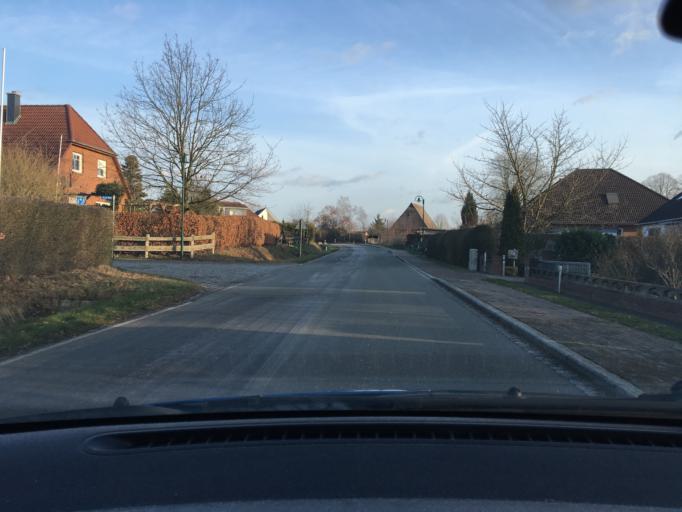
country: DE
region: Schleswig-Holstein
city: Witzeeze
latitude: 53.4538
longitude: 10.6025
